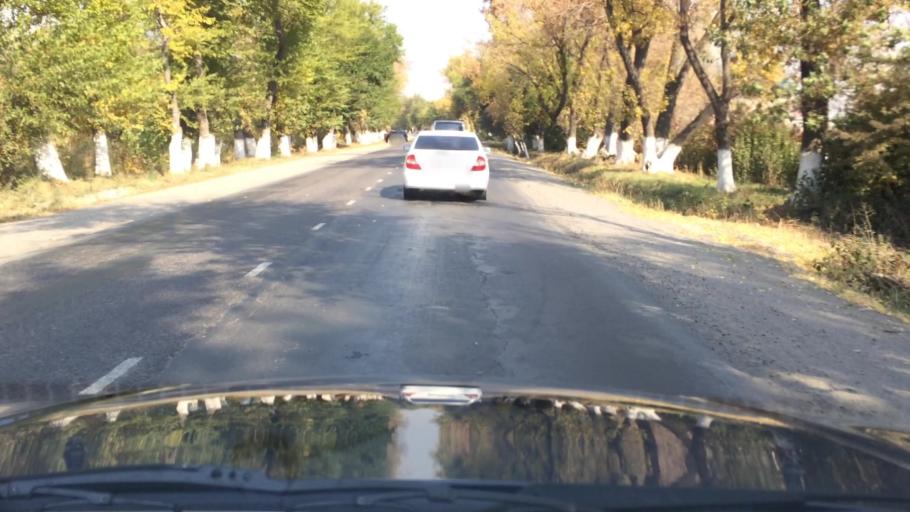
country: KG
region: Chuy
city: Lebedinovka
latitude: 42.9114
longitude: 74.6878
